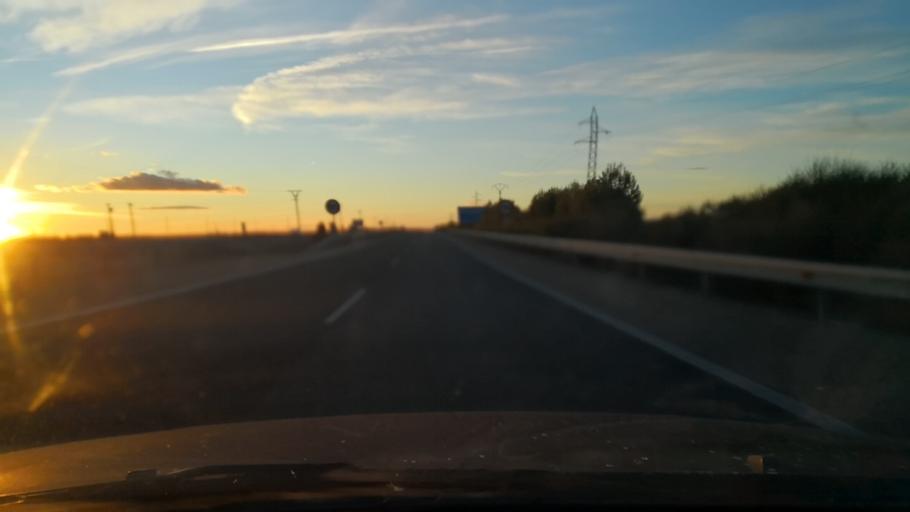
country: ES
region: Castille and Leon
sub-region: Provincia de Valladolid
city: Torrecilla de la Abadesa
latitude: 41.5050
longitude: -5.0498
